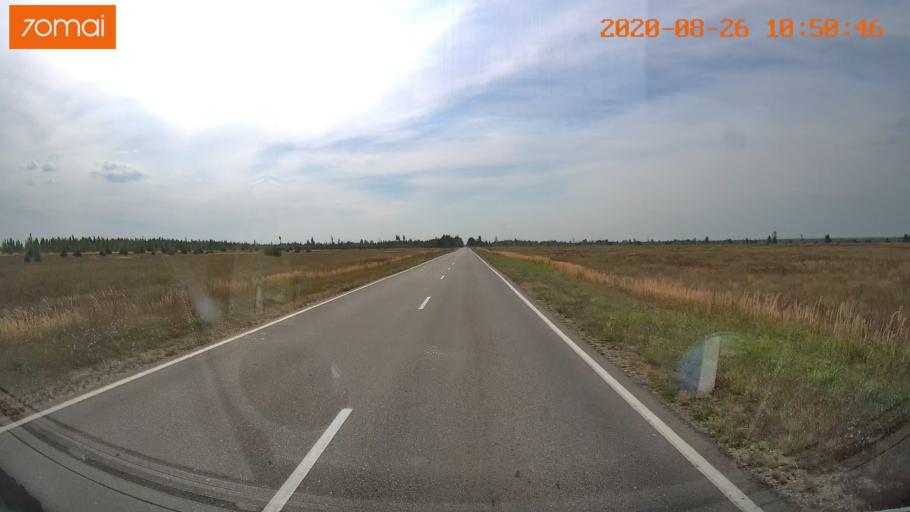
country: RU
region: Rjazan
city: Lashma
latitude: 54.6826
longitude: 41.1561
